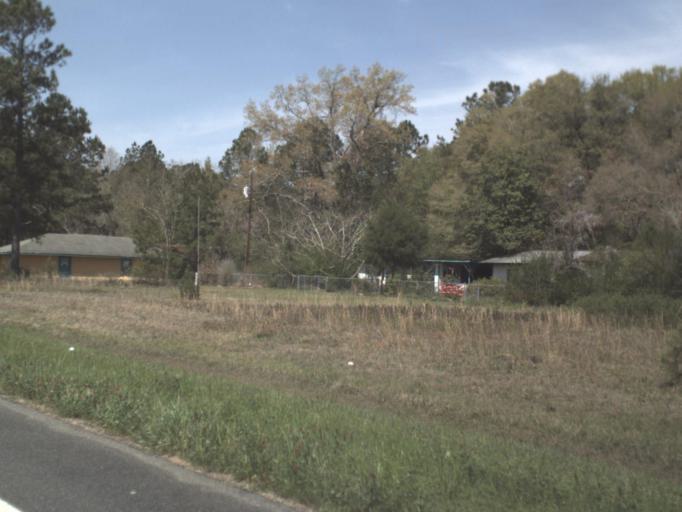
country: US
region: Florida
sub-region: Holmes County
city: Bonifay
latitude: 30.7617
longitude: -85.8684
